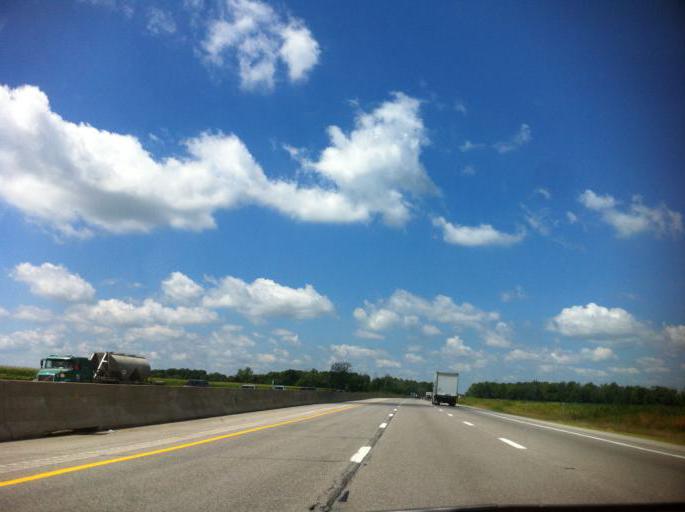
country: US
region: Ohio
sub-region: Sandusky County
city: Stony Prairie
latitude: 41.4234
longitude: -83.1776
